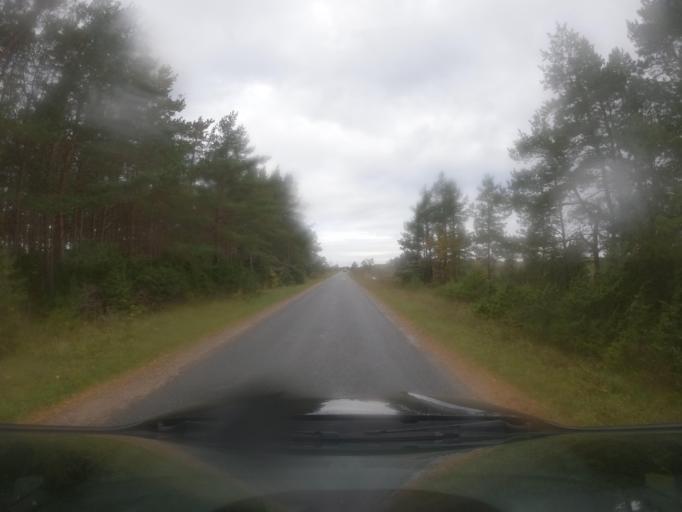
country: EE
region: Saare
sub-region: Kuressaare linn
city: Kuressaare
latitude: 58.4421
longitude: 21.9859
